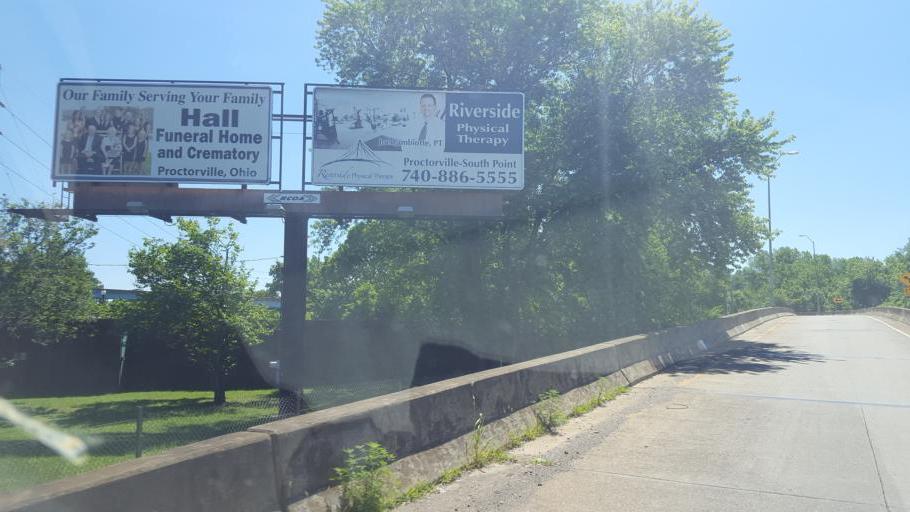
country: US
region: West Virginia
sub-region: Cabell County
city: Huntington
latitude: 38.4280
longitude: -82.3929
